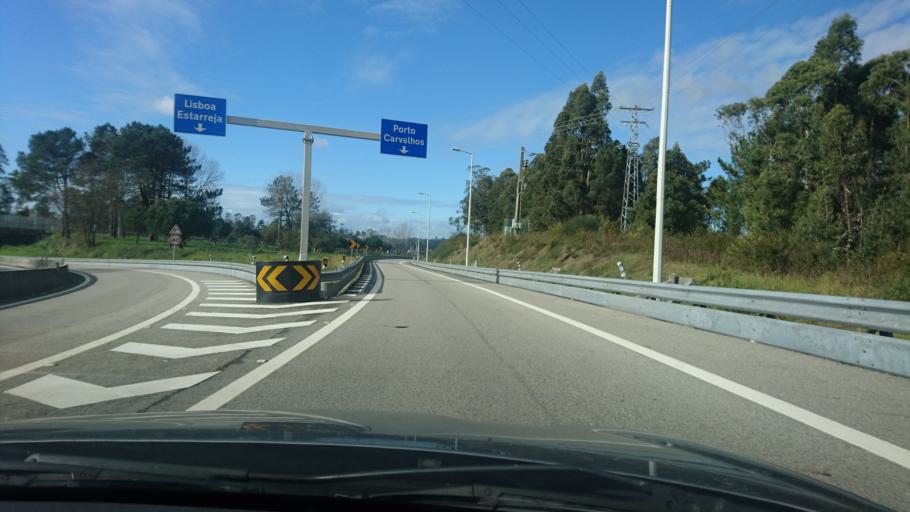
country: PT
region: Aveiro
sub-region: Santa Maria da Feira
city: Feira
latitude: 40.9296
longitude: -8.5672
